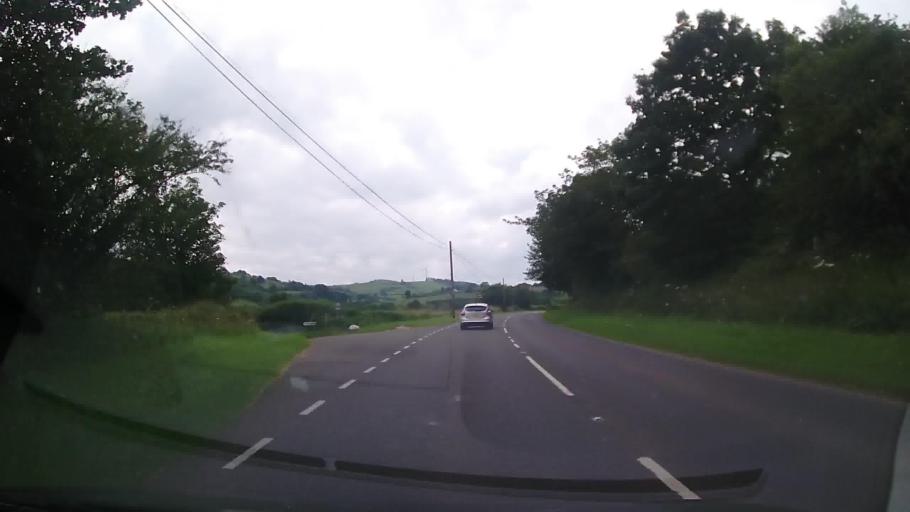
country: GB
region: Wales
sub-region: Denbighshire
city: Llandrillo
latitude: 52.9727
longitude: -3.4434
